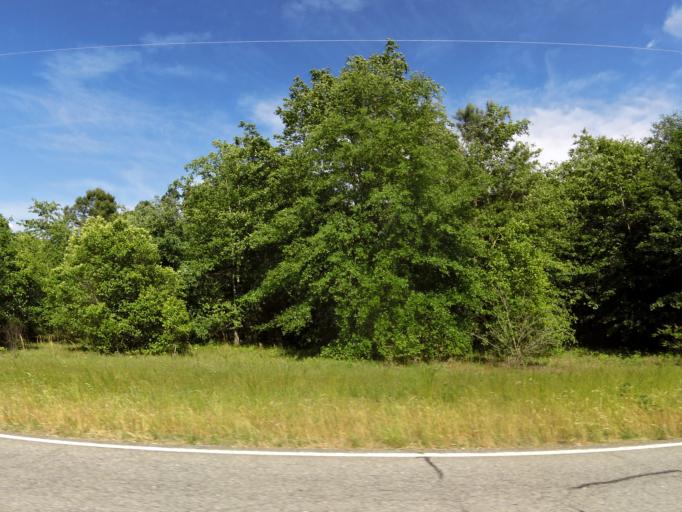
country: US
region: South Carolina
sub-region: Bamberg County
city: Denmark
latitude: 33.2149
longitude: -81.1749
